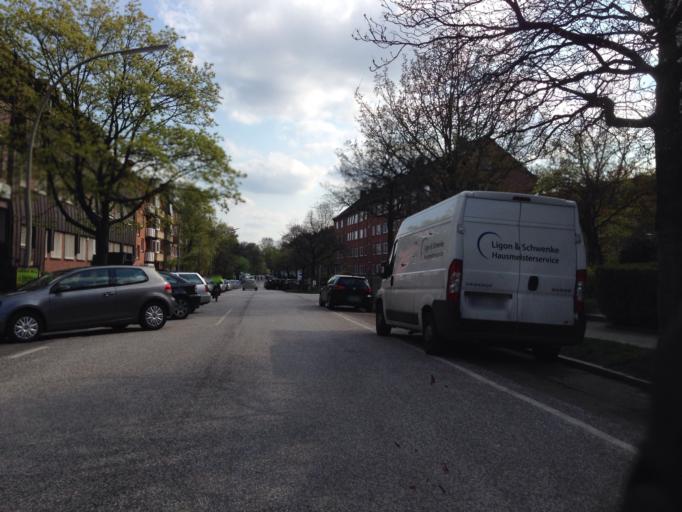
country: DE
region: Hamburg
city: Borgfelde
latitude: 53.5746
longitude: 10.0444
